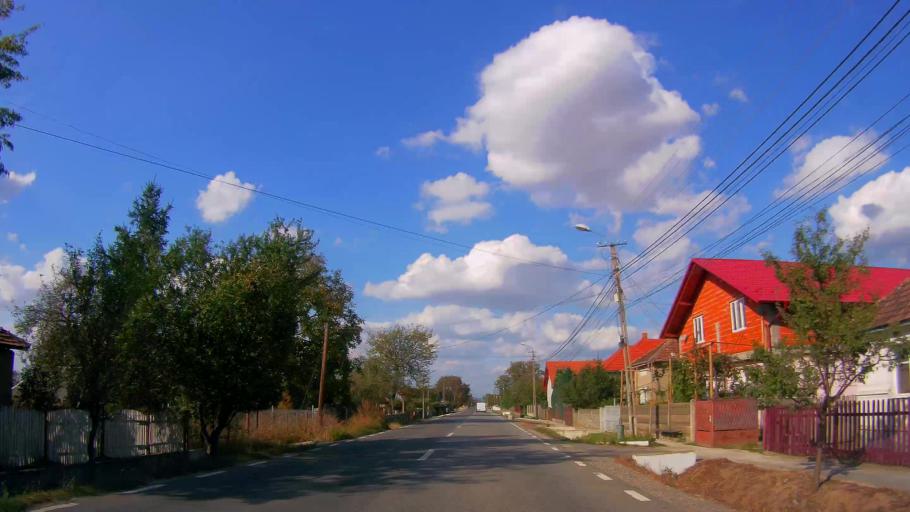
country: RO
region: Satu Mare
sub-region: Comuna Turulung
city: Draguseni
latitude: 47.8963
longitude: 23.0745
